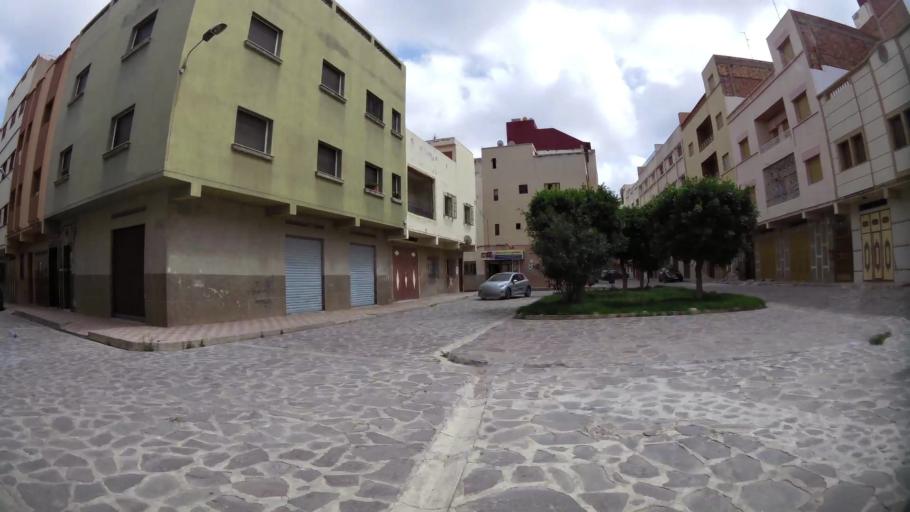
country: MA
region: Oriental
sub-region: Nador
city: Nador
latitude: 35.1735
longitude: -2.9313
